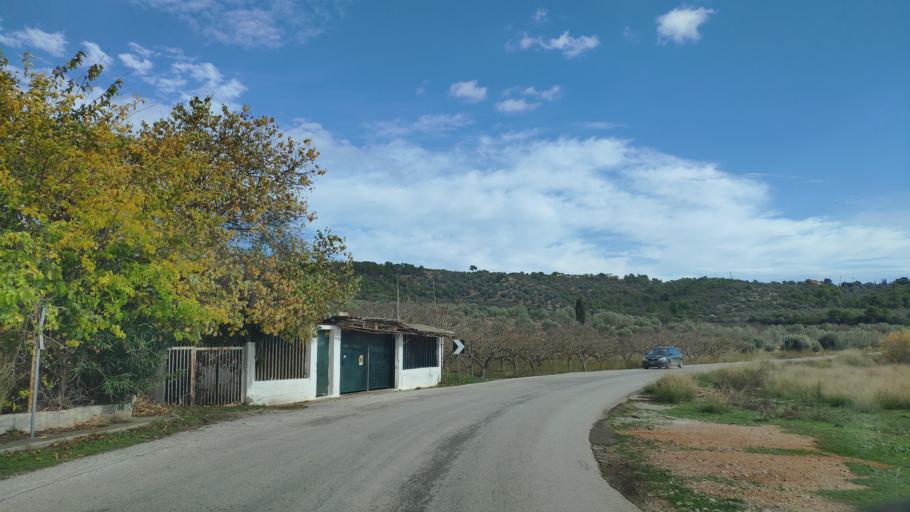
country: GR
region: Attica
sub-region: Nomarchia Anatolikis Attikis
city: Artemida
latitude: 37.9286
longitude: 23.9924
